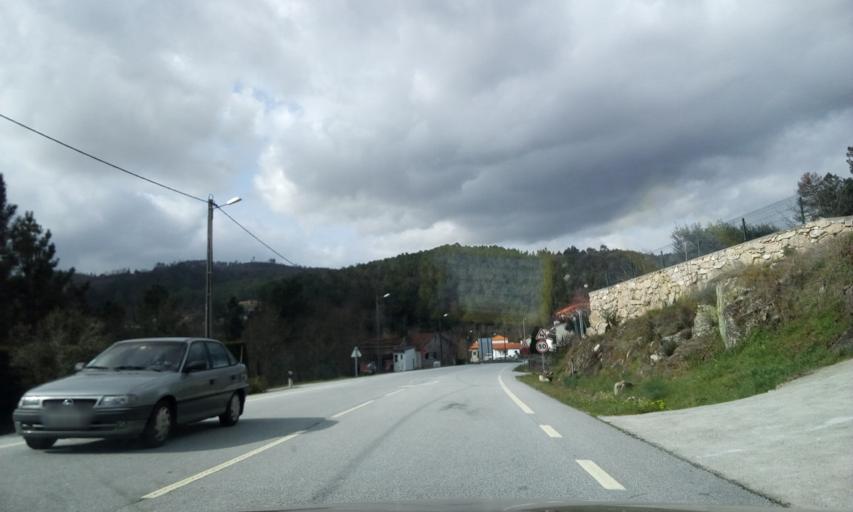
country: PT
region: Viseu
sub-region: Mangualde
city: Mangualde
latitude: 40.6464
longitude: -7.7318
